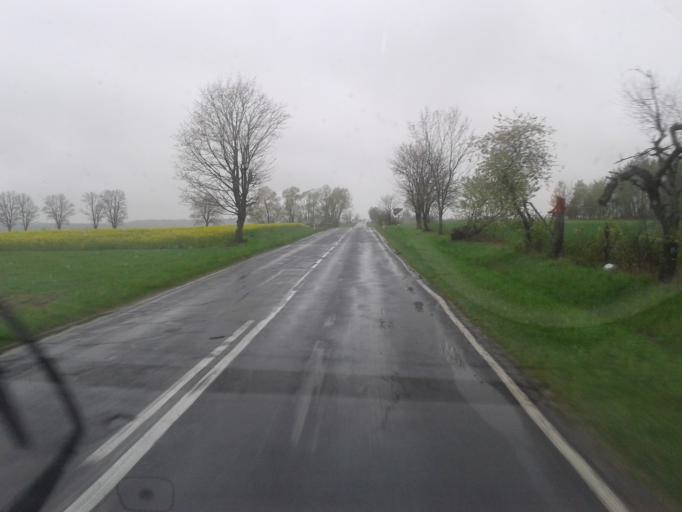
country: PL
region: Subcarpathian Voivodeship
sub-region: Powiat lubaczowski
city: Nowe Siolo
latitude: 50.2876
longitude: 23.1850
